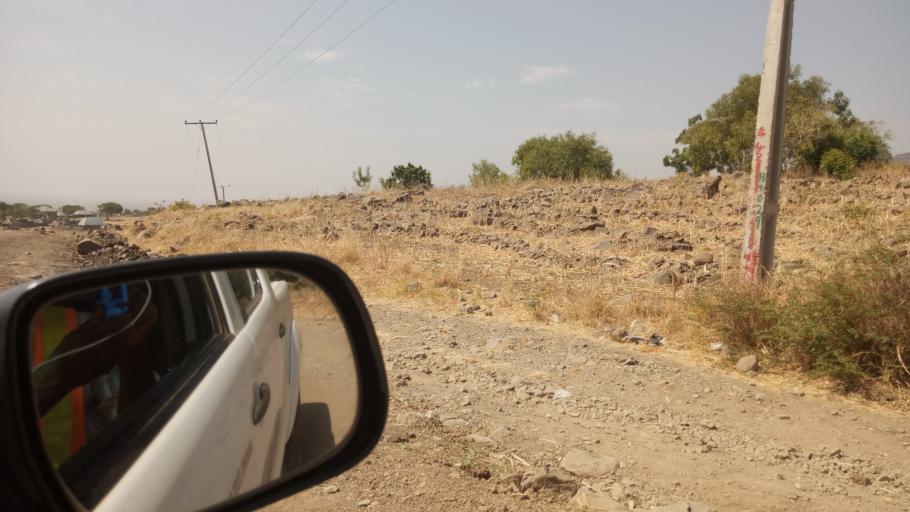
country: NG
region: Adamawa
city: Numan
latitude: 9.7012
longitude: 11.9234
